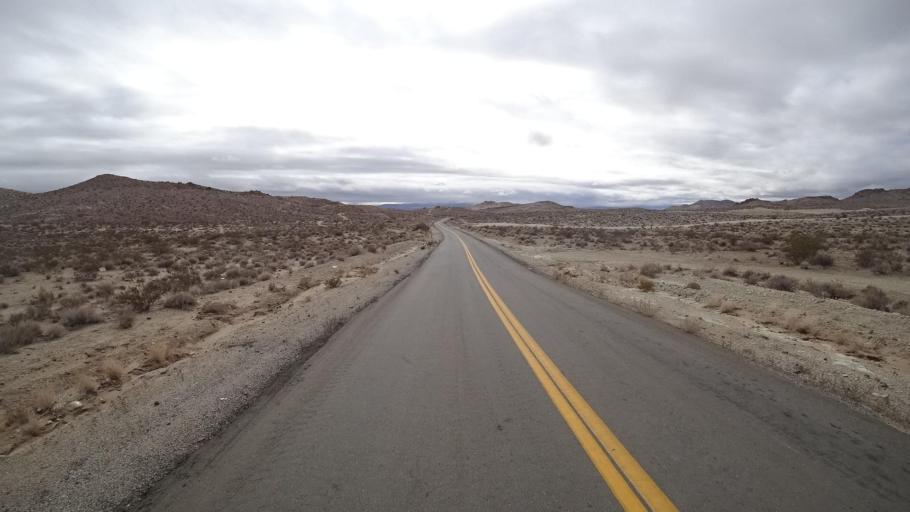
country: US
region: California
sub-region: Kern County
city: Rosamond
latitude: 34.9191
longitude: -118.2140
